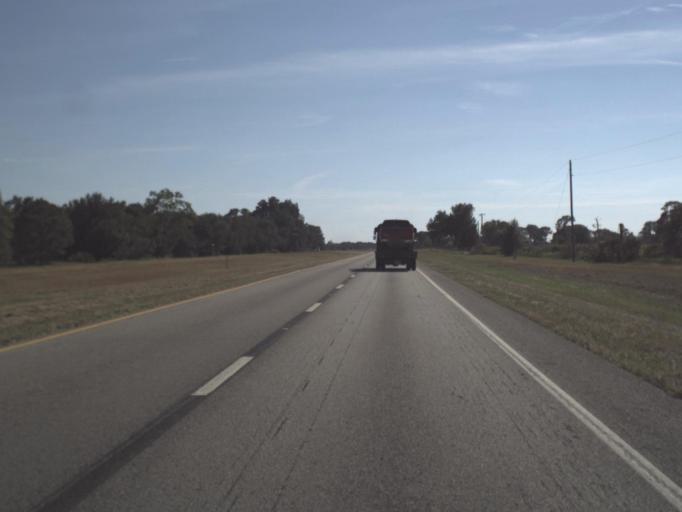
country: US
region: Florida
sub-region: Highlands County
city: Placid Lakes
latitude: 27.0934
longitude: -81.3337
